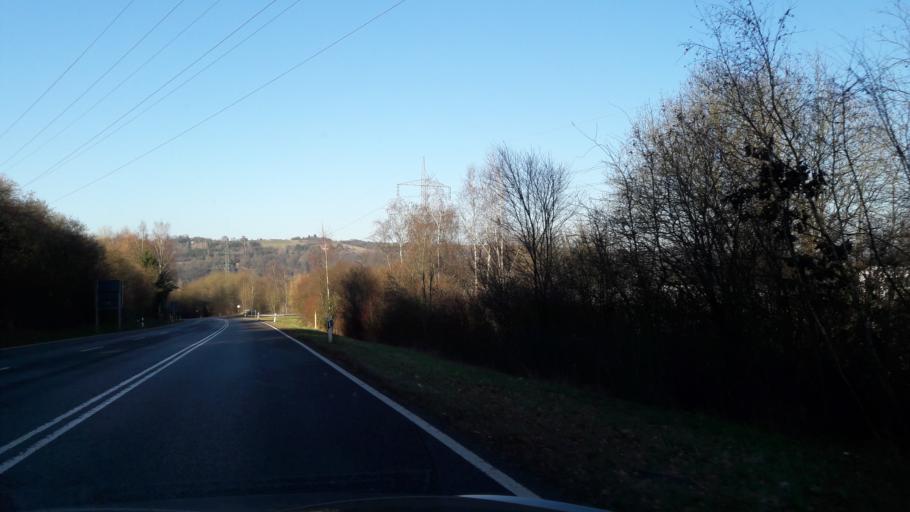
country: DE
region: Saarland
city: Hangard
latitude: 49.3691
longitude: 7.2054
